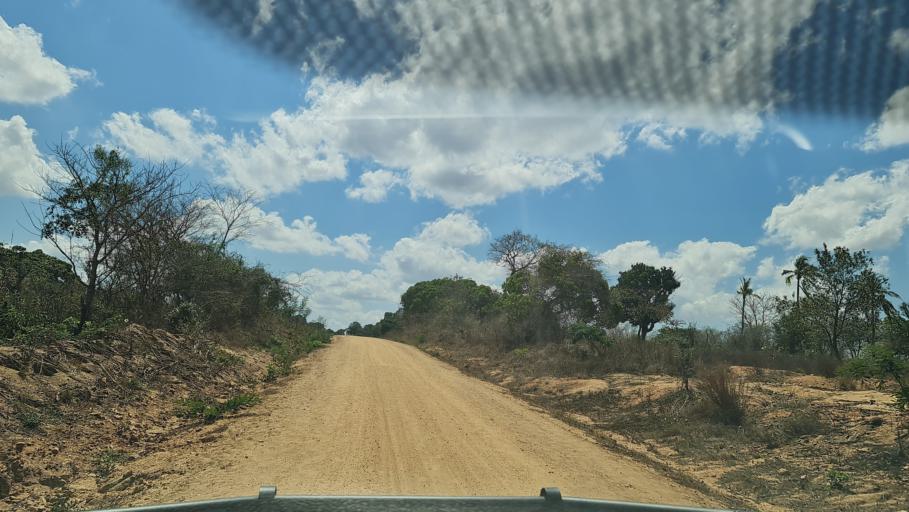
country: MZ
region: Nampula
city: Nacala
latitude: -14.1749
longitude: 40.2357
